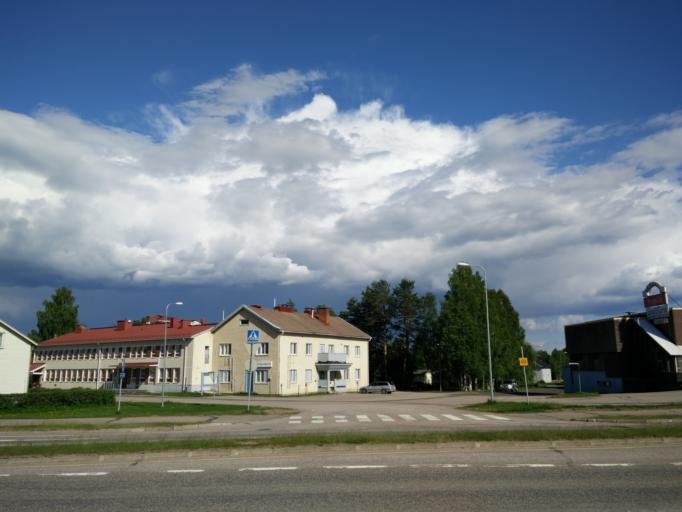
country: FI
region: Lapland
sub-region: Torniolaakso
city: Pello
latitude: 66.7743
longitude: 23.9648
